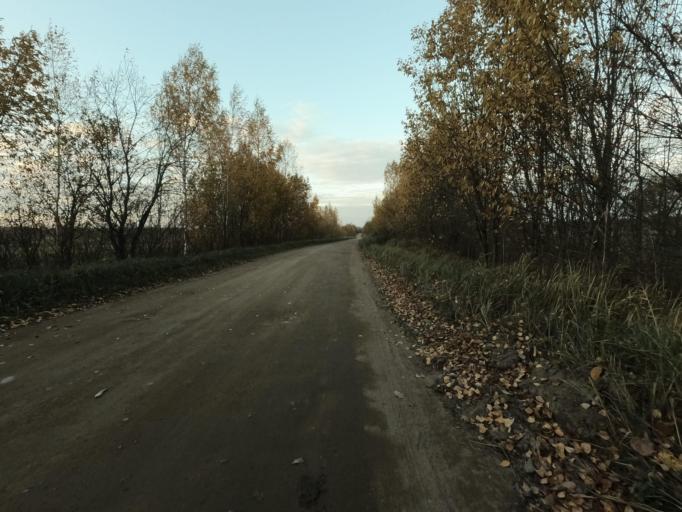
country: RU
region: Leningrad
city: Mga
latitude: 59.7976
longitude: 31.2001
